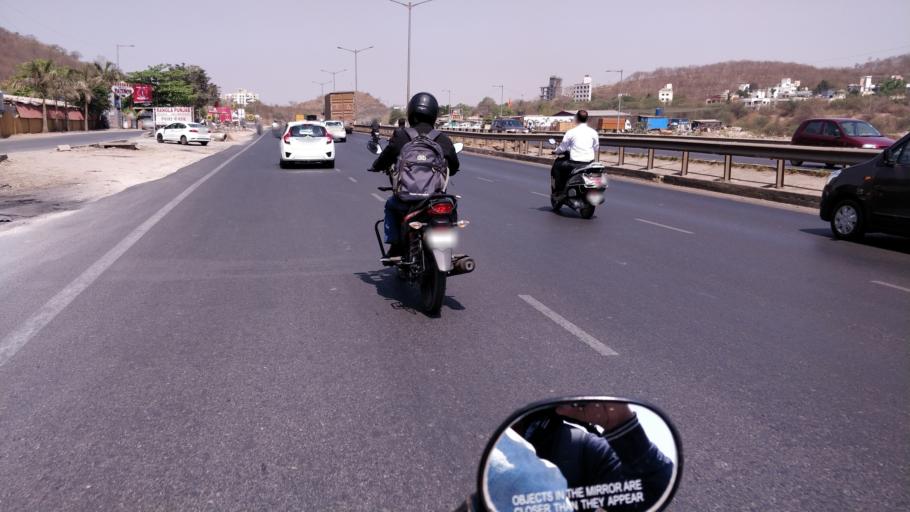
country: IN
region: Maharashtra
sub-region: Pune Division
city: Shivaji Nagar
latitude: 18.5423
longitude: 73.7771
